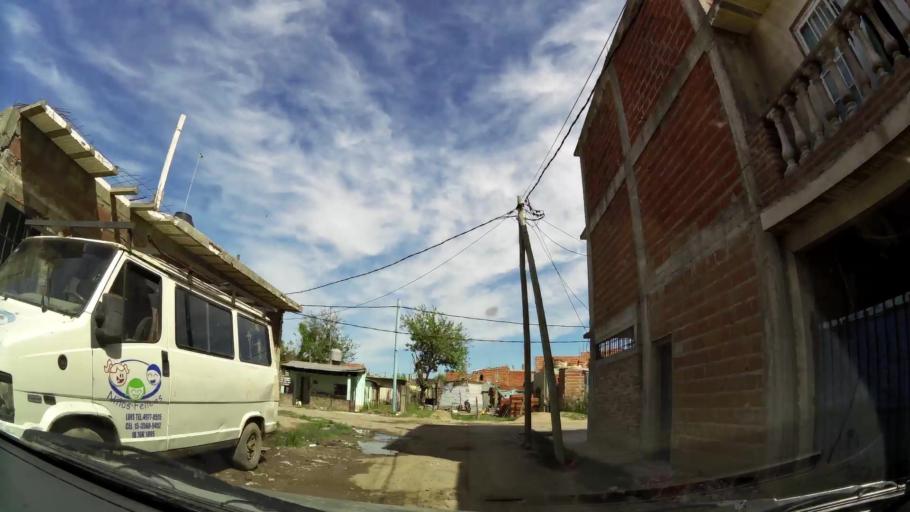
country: AR
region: Buenos Aires
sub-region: Partido de Quilmes
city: Quilmes
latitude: -34.7782
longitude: -58.2970
